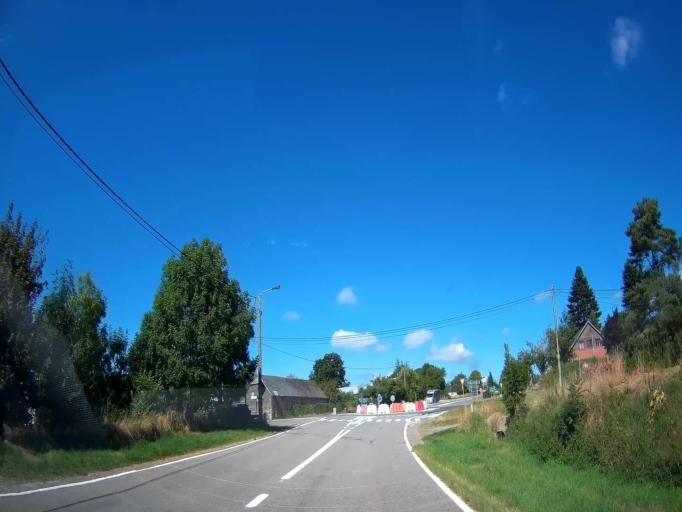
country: BE
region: Wallonia
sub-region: Province du Luxembourg
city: Bertogne
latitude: 50.1247
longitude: 5.6155
